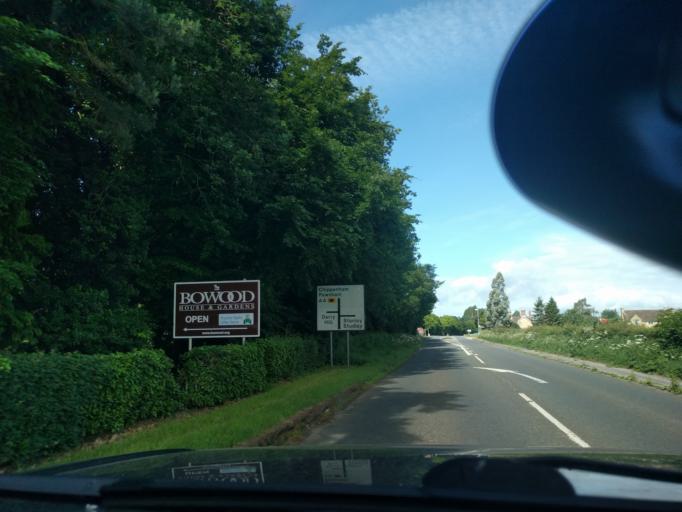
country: GB
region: England
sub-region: Wiltshire
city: Bremhill
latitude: 51.4386
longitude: -2.0498
